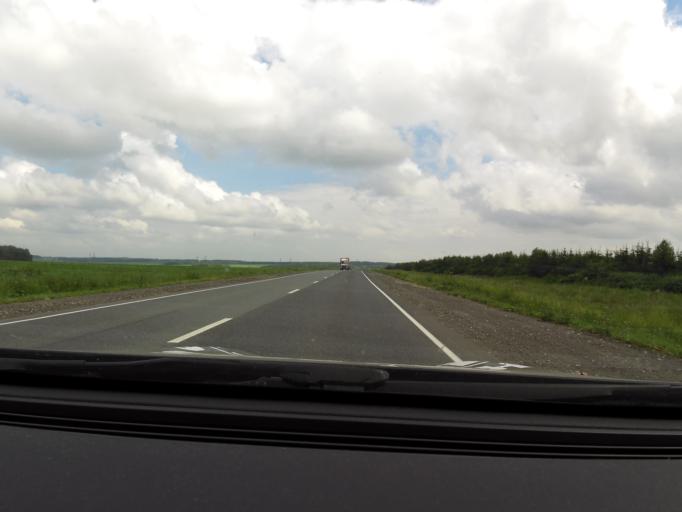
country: RU
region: Perm
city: Suksun
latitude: 57.1602
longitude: 57.1896
